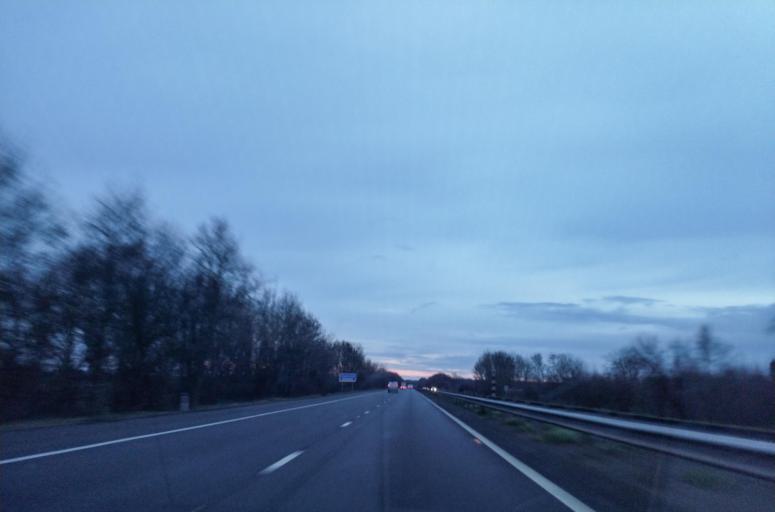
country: GB
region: England
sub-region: Kent
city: Sittingbourne
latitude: 51.2975
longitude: 0.7542
